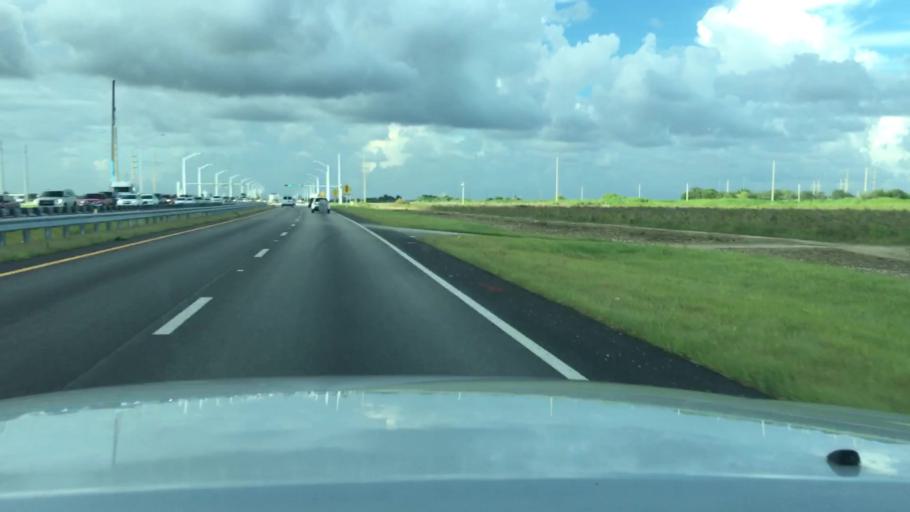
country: US
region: Florida
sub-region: Miami-Dade County
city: Country Walk
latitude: 25.6348
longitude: -80.4795
